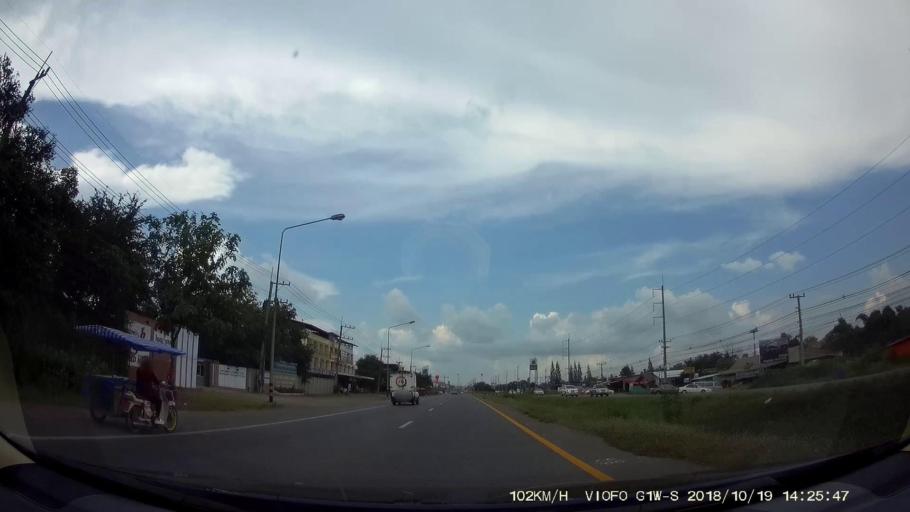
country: TH
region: Chaiyaphum
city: Kaeng Khro
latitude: 16.0987
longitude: 102.2626
